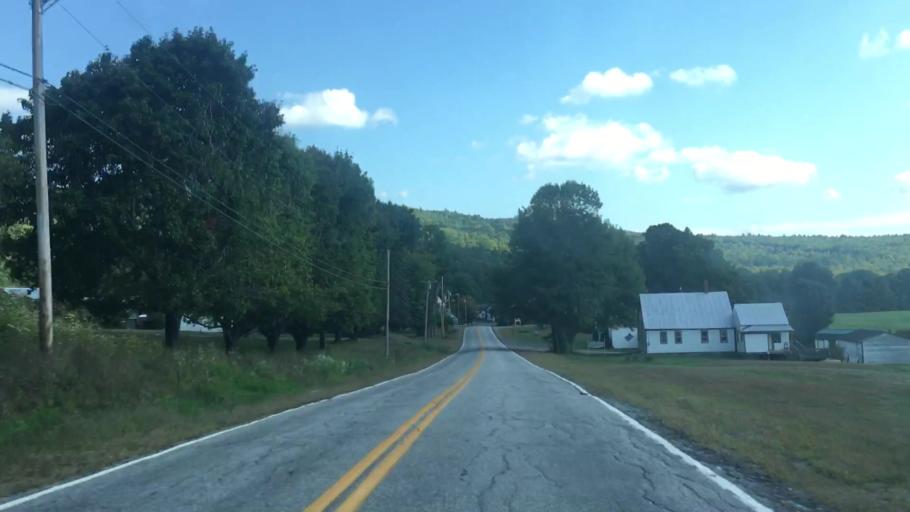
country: US
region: Maine
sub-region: Kennebec County
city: Mount Vernon
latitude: 44.5353
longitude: -69.9874
